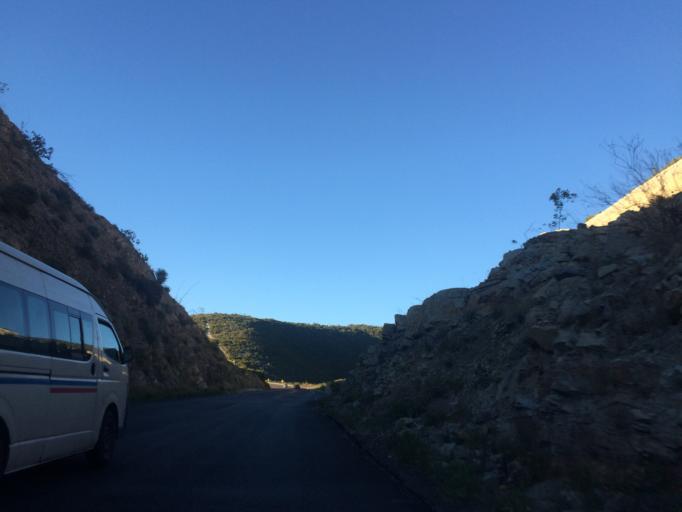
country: MX
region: Puebla
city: Chapuco
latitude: 18.6620
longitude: -97.4567
